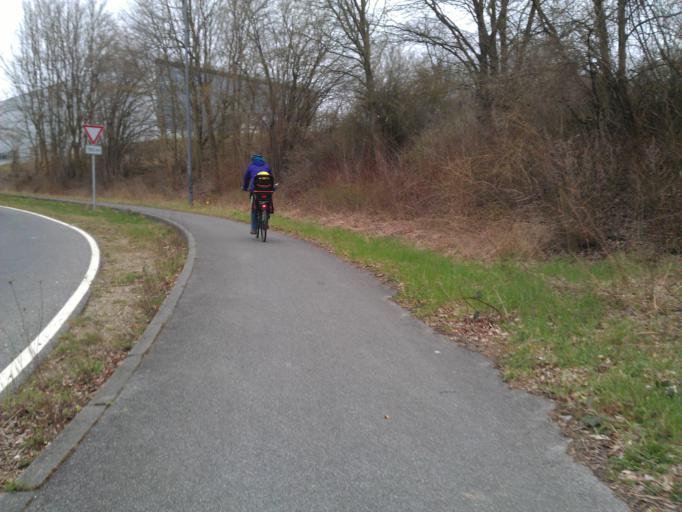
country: DE
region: North Rhine-Westphalia
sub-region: Regierungsbezirk Koln
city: Aachen
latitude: 50.7887
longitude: 6.0511
